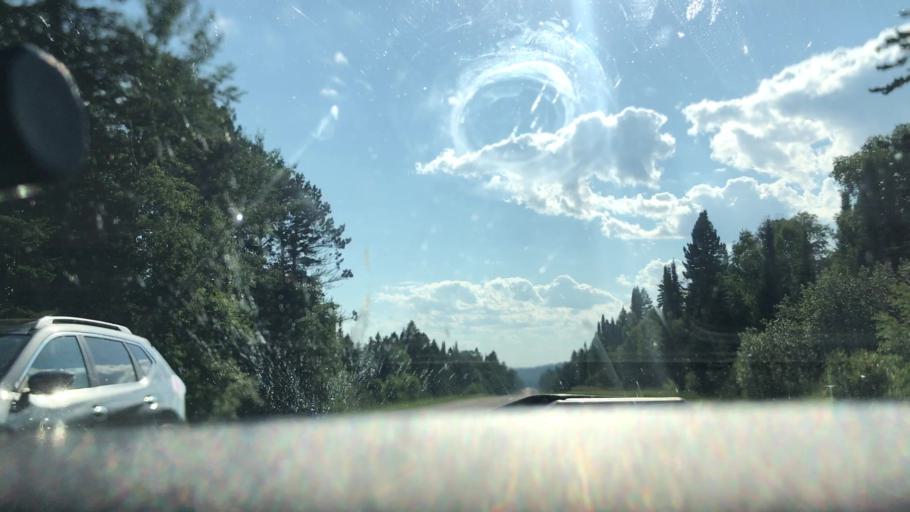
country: US
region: Minnesota
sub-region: Cook County
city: Grand Marais
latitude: 47.7964
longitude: -90.1266
